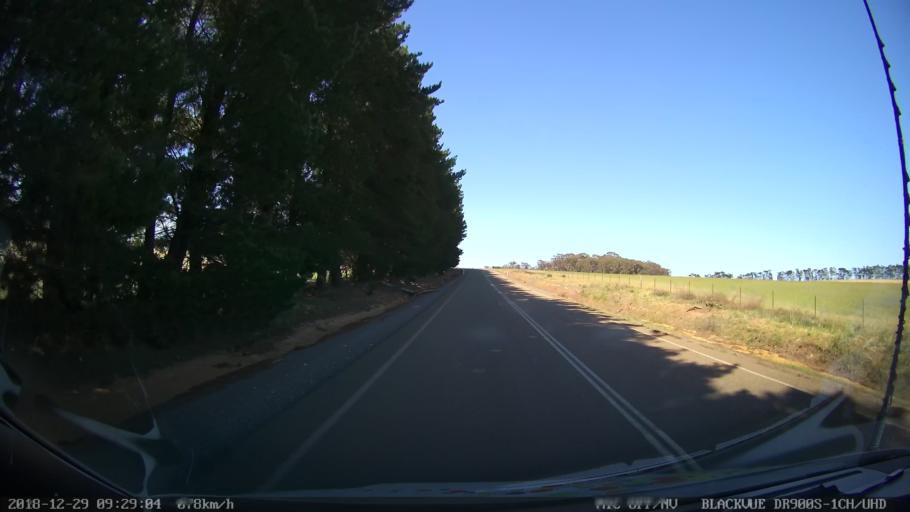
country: AU
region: New South Wales
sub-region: Upper Lachlan Shire
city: Crookwell
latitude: -34.5856
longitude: 149.3773
